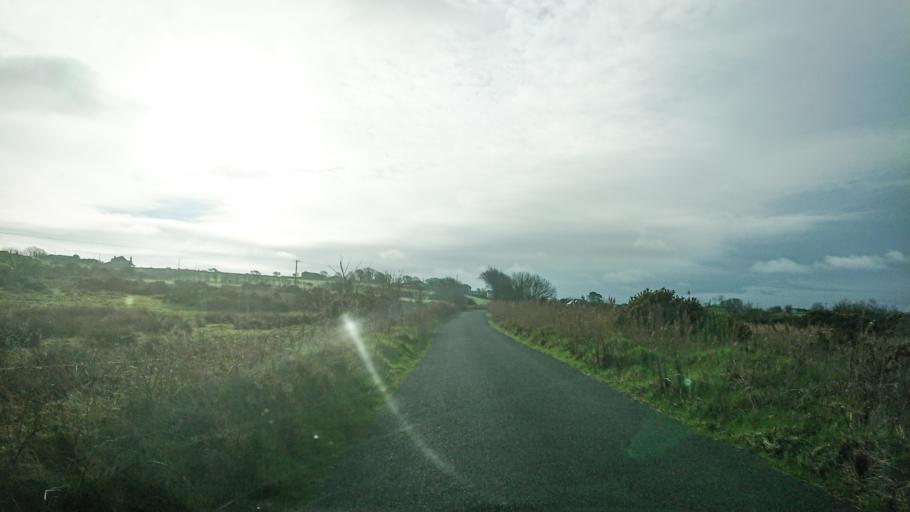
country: IE
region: Munster
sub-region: Waterford
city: Tra Mhor
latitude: 52.1603
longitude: -7.1882
